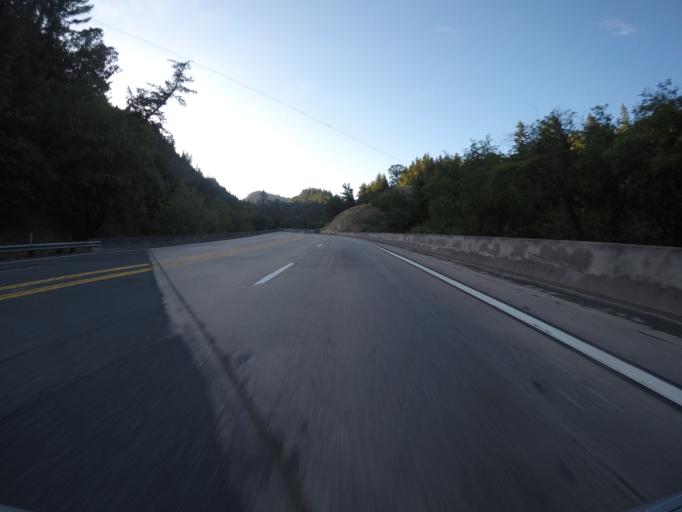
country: US
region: California
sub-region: Mendocino County
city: Brooktrails
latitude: 39.5630
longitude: -123.4334
